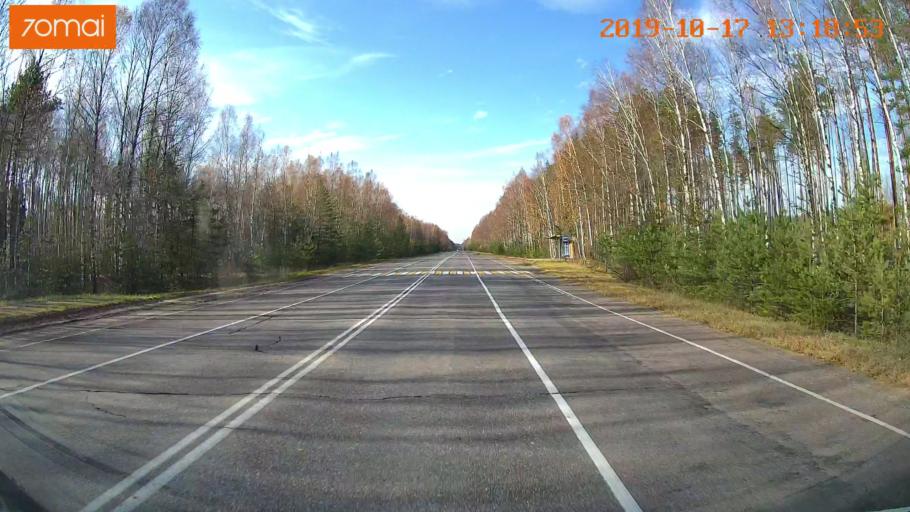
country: RU
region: Rjazan
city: Gus'-Zheleznyy
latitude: 55.0659
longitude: 41.0872
